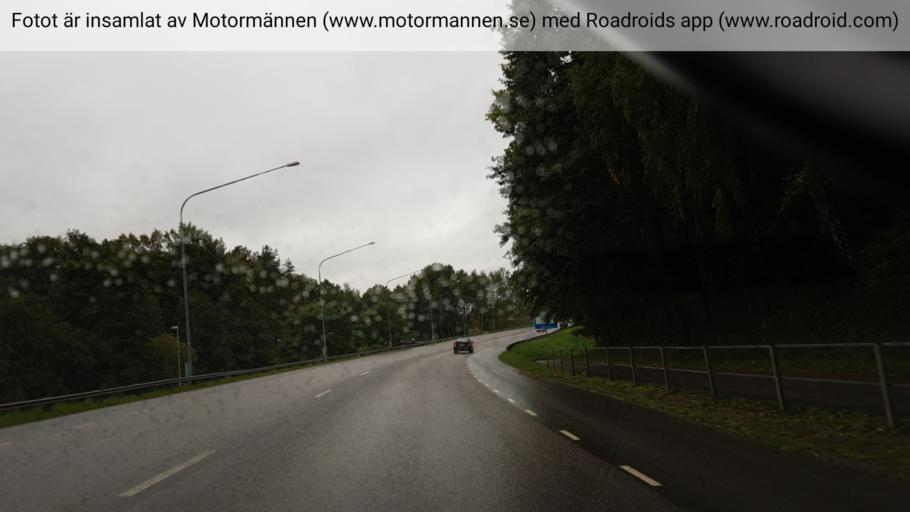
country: SE
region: Vaestra Goetaland
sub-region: Skovde Kommun
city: Skoevde
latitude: 58.4171
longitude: 13.8692
